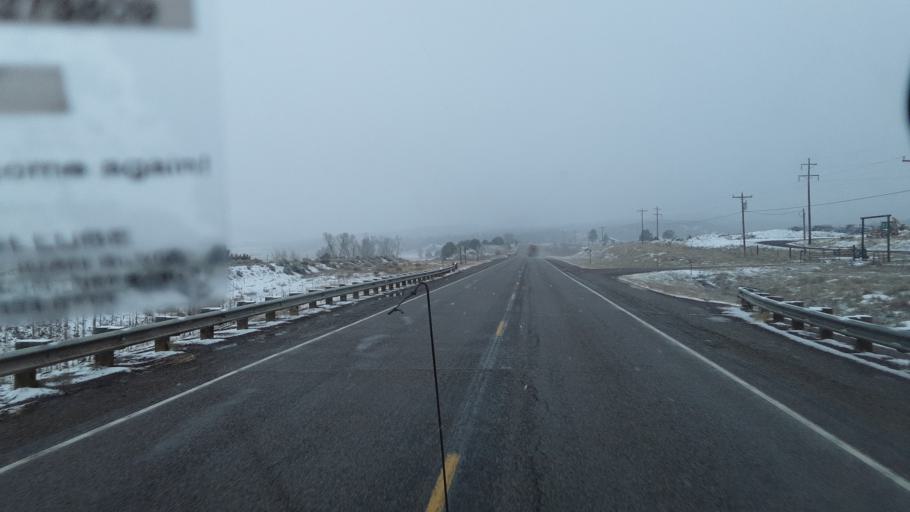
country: US
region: New Mexico
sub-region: Rio Arriba County
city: Tierra Amarilla
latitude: 36.7728
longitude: -106.5562
